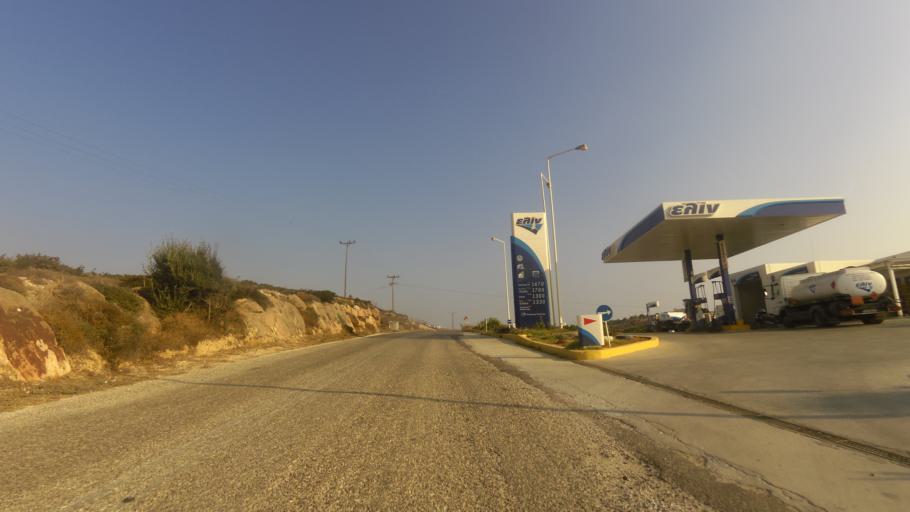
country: GR
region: South Aegean
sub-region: Nomos Kykladon
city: Antiparos
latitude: 37.0285
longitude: 25.0758
